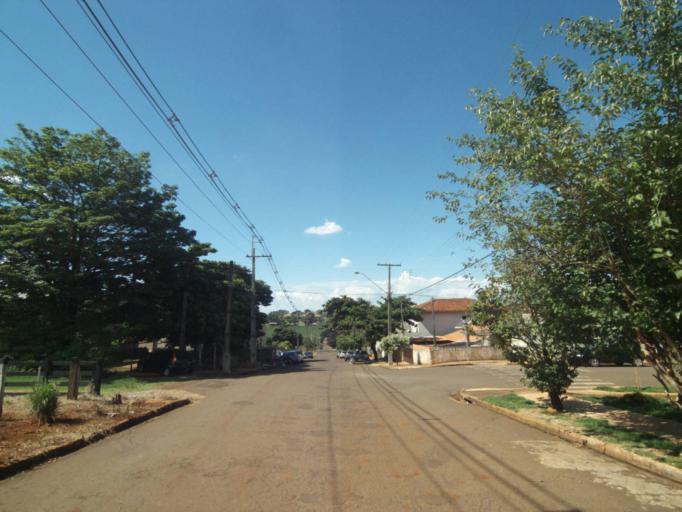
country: BR
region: Parana
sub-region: Sertanopolis
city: Sertanopolis
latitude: -23.0427
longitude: -50.8220
